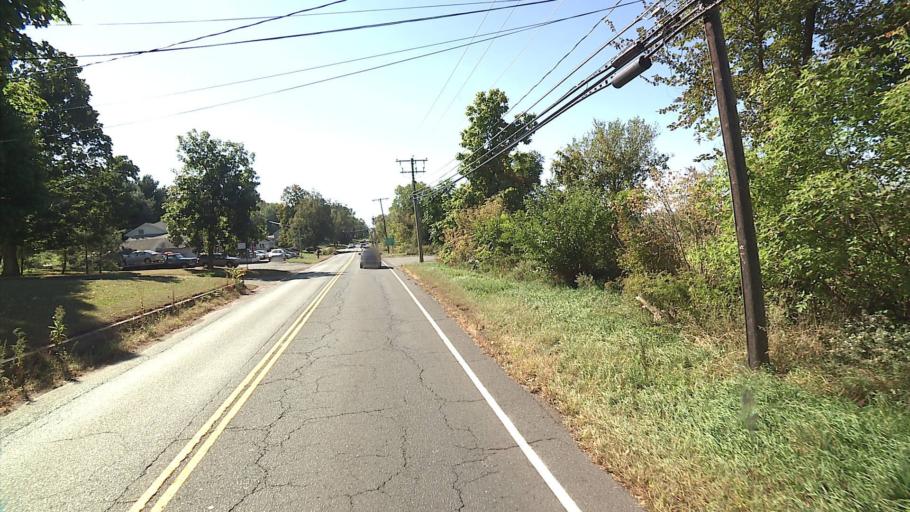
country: US
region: Connecticut
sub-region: Tolland County
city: Ellington
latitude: 41.9124
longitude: -72.4542
